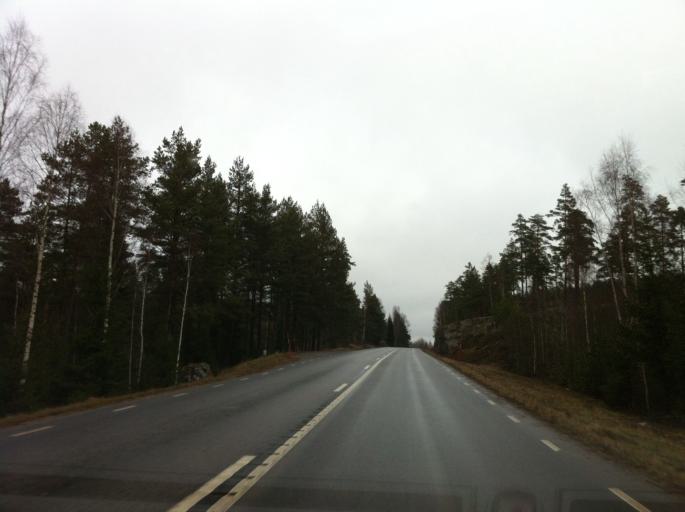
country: SE
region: Kalmar
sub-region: Vimmerby Kommun
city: Sodra Vi
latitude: 57.8732
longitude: 15.7511
